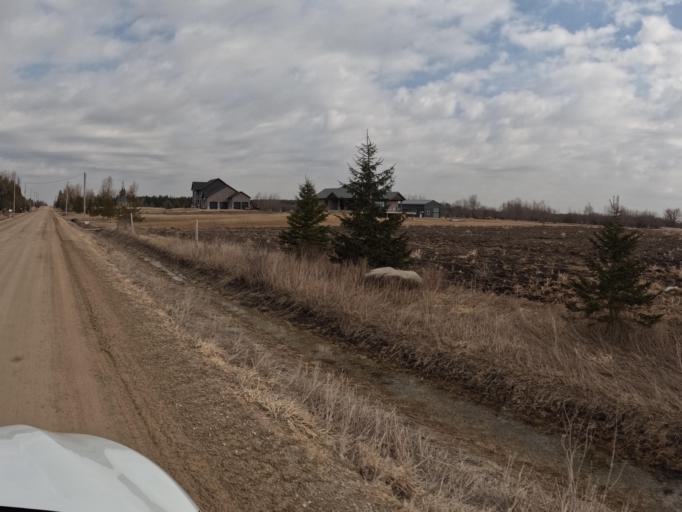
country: CA
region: Ontario
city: Orangeville
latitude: 43.9281
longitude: -80.2196
